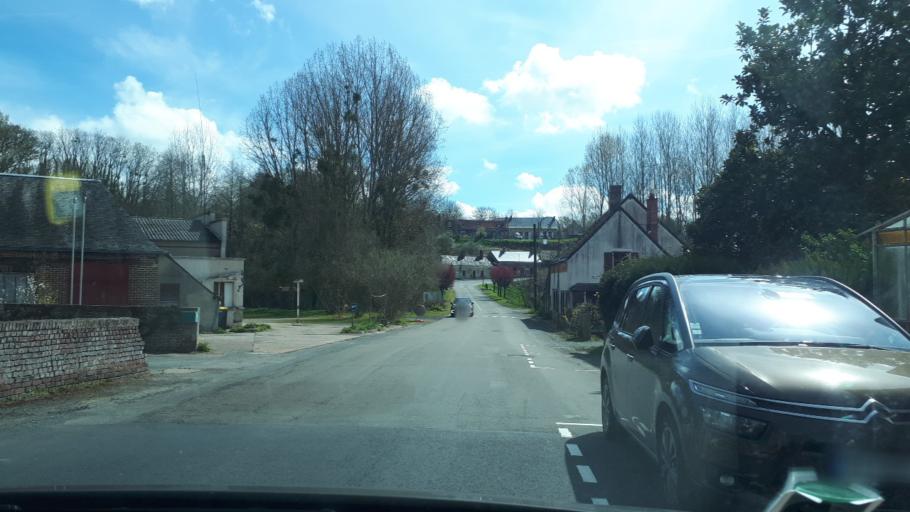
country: FR
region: Pays de la Loire
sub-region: Departement de la Sarthe
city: Bouloire
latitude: 47.9033
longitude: 0.5752
